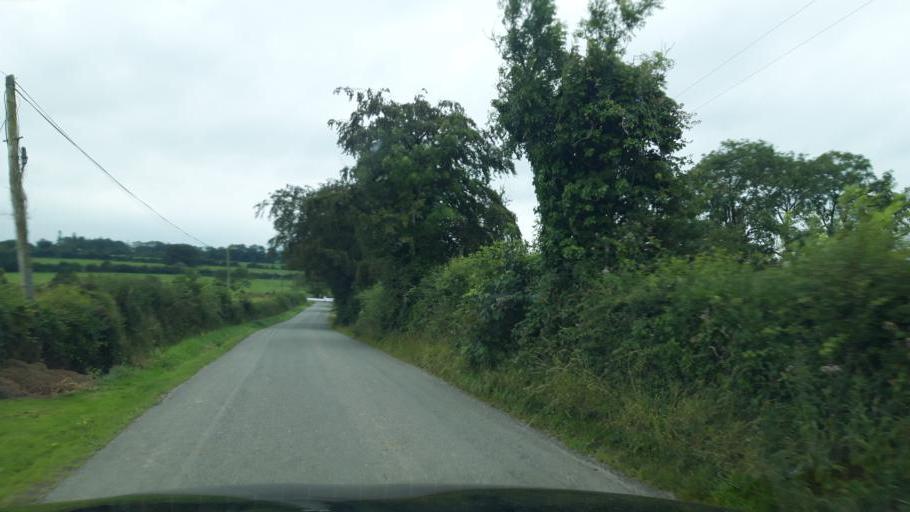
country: IE
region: Leinster
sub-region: Kilkenny
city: Ballyragget
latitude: 52.7057
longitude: -7.4065
